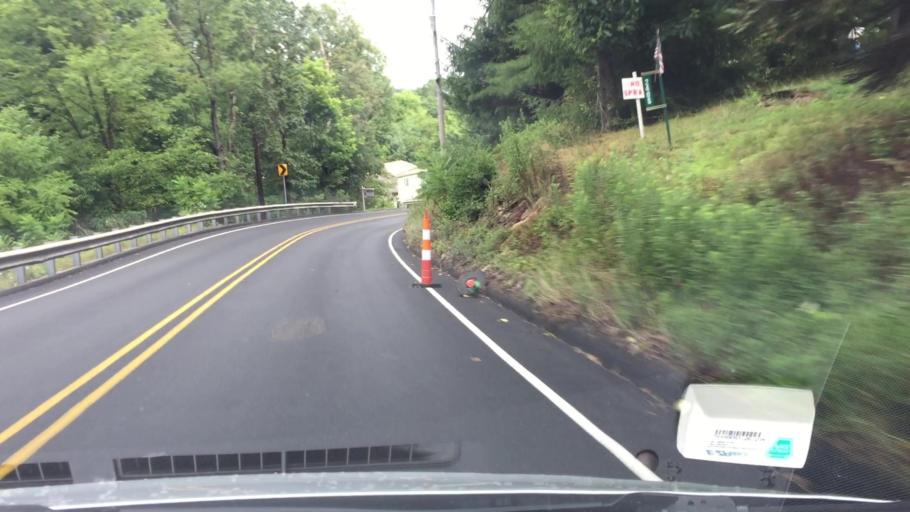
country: US
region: Pennsylvania
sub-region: Allegheny County
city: Gibsonia
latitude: 40.6050
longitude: -79.9684
